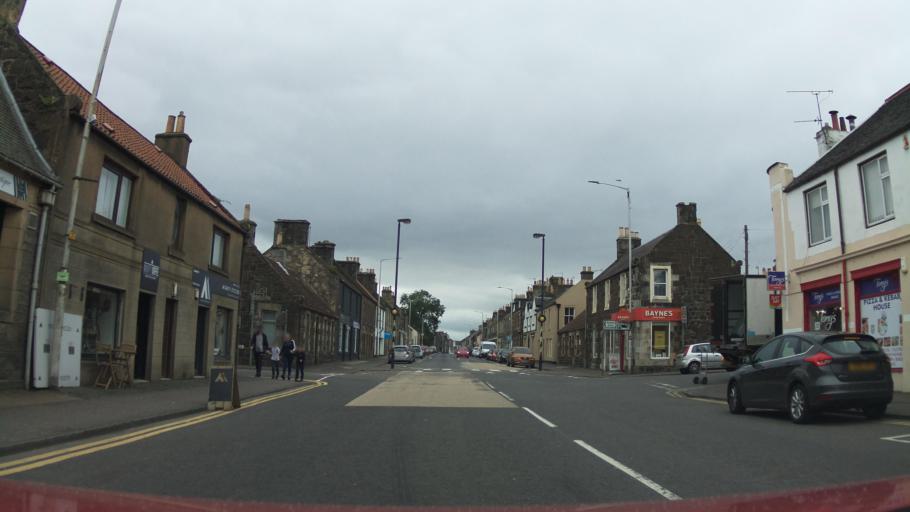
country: GB
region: Scotland
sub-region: Fife
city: Leslie
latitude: 56.2023
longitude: -3.2110
